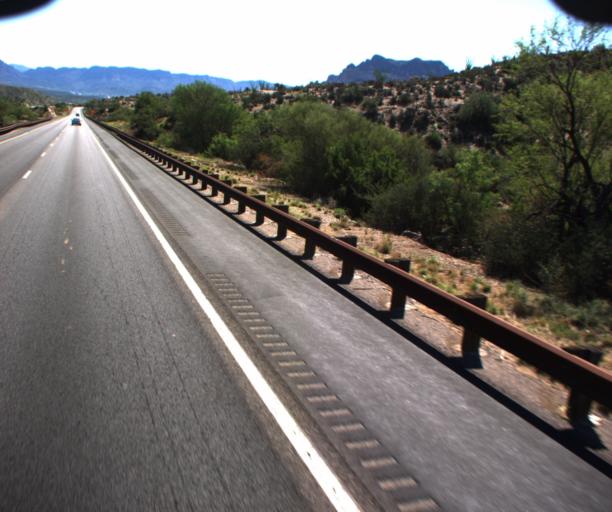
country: US
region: Arizona
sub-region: Pinal County
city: Gold Camp
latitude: 33.2729
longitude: -111.2125
